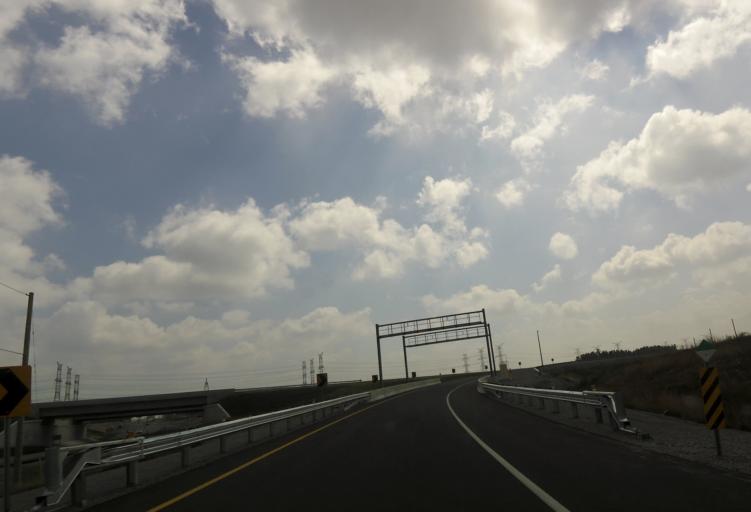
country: CA
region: Ontario
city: Oshawa
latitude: 43.9838
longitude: -78.8693
